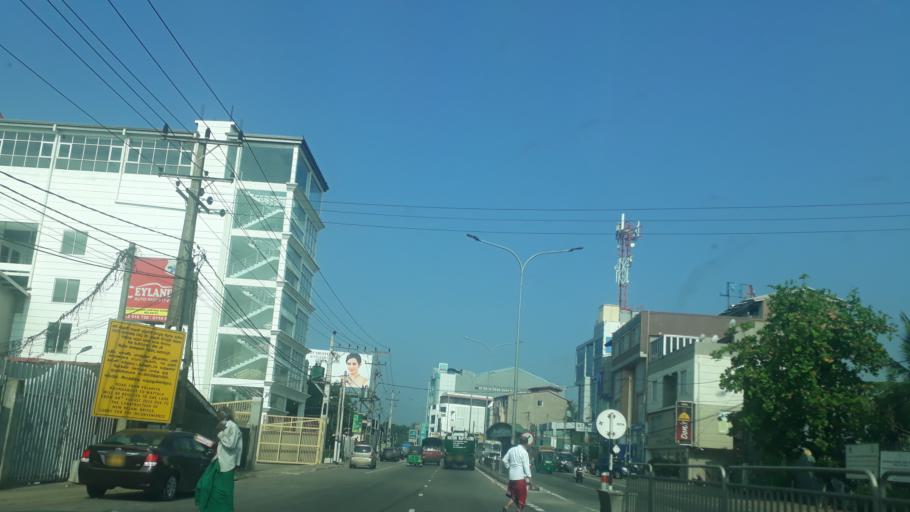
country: LK
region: Western
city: Kelaniya
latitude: 6.9672
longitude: 79.9066
